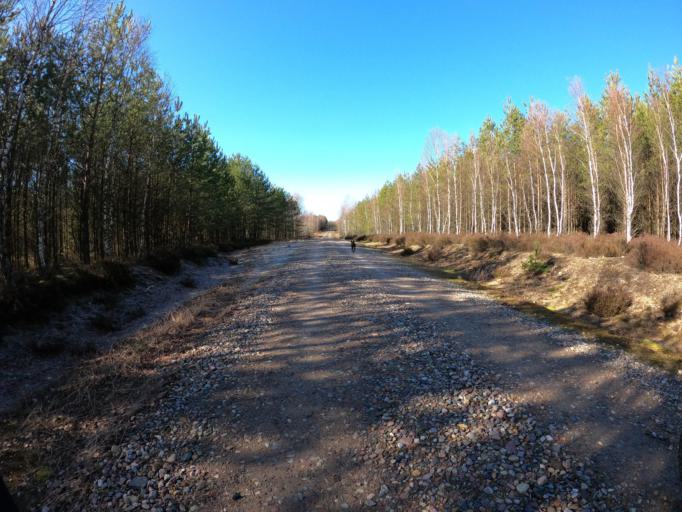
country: PL
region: Greater Poland Voivodeship
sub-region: Powiat zlotowski
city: Sypniewo
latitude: 53.5333
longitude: 16.6118
